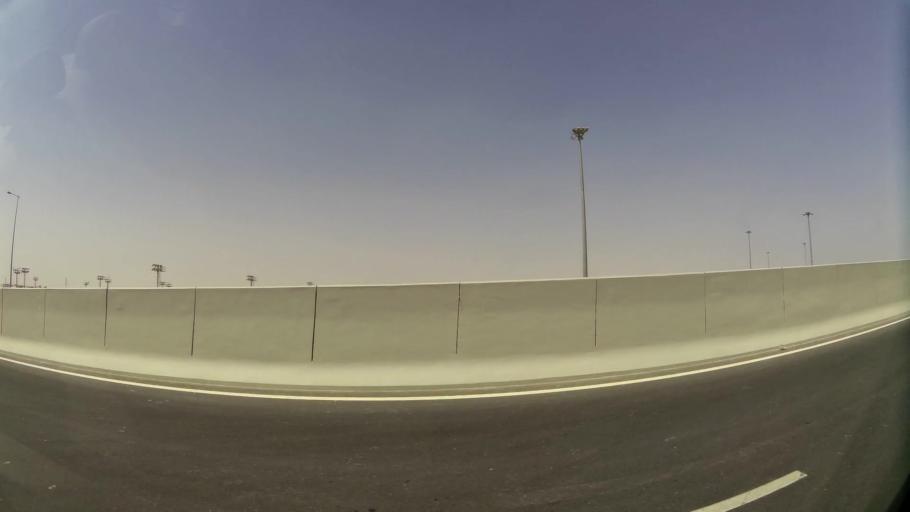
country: QA
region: Baladiyat Umm Salal
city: Umm Salal Muhammad
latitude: 25.3781
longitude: 51.4381
